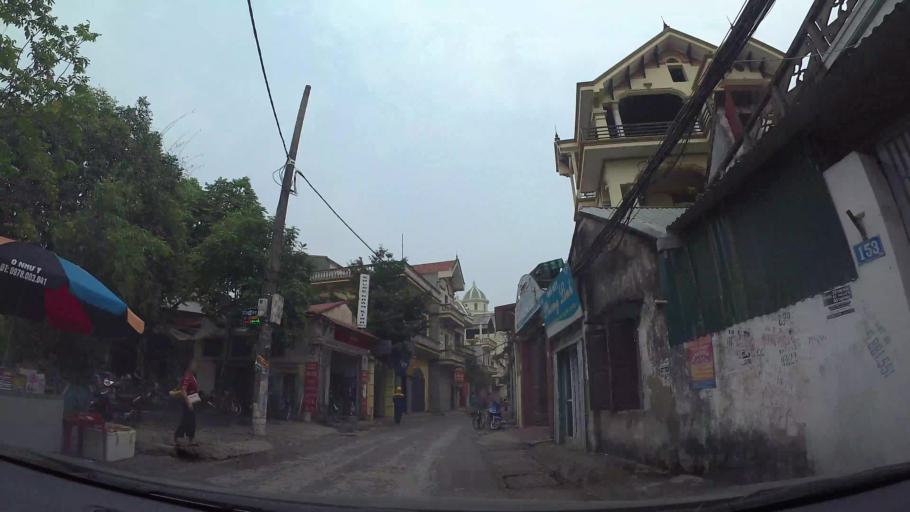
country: VN
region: Ha Noi
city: Van Dien
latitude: 20.9701
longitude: 105.8702
